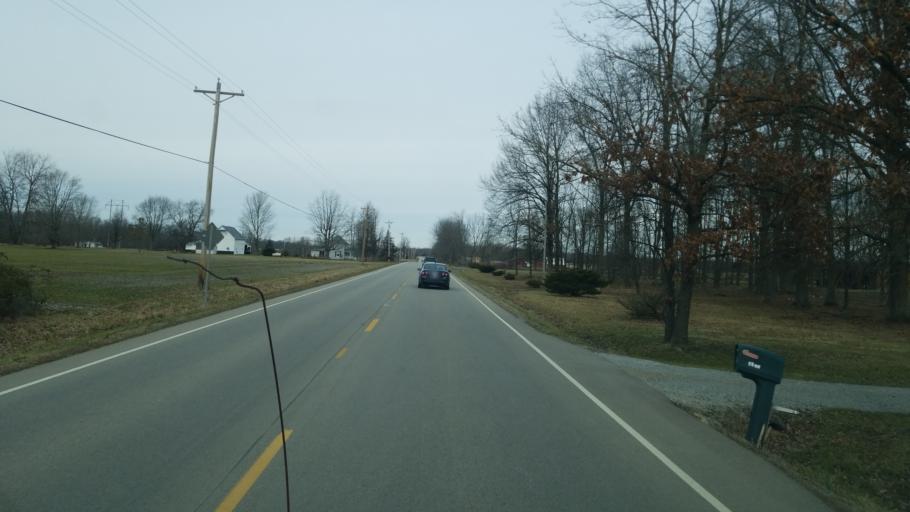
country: US
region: Ohio
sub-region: Highland County
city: Hillsboro
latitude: 39.0881
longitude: -83.6821
